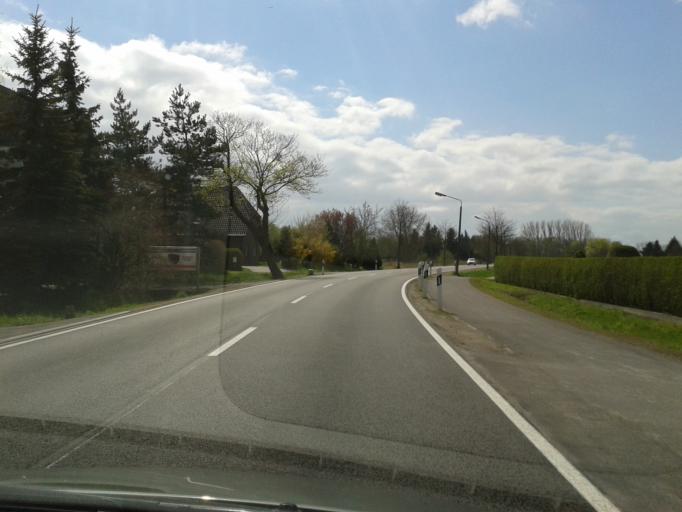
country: DE
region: Lower Saxony
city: Lubbow
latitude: 52.8848
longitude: 11.1744
